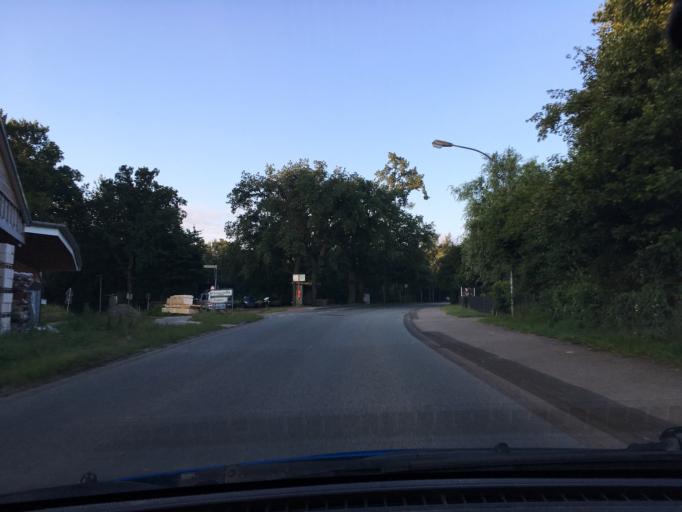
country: DE
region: Lower Saxony
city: Harmstorf
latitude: 53.3859
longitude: 10.0380
